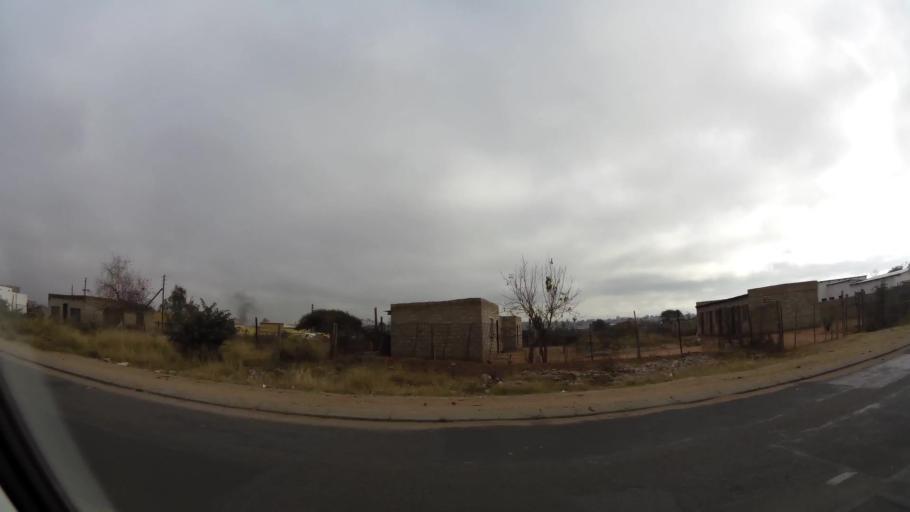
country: ZA
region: Limpopo
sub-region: Capricorn District Municipality
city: Polokwane
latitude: -23.8335
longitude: 29.3817
